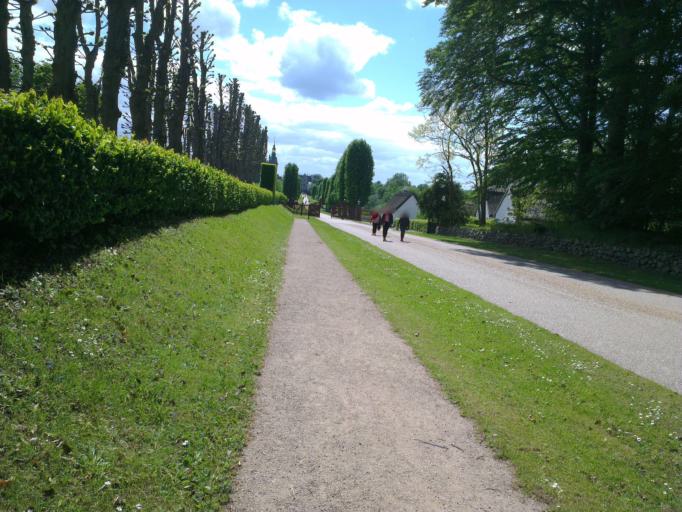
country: DK
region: Capital Region
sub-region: Hillerod Kommune
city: Hillerod
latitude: 55.9402
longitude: 12.3057
